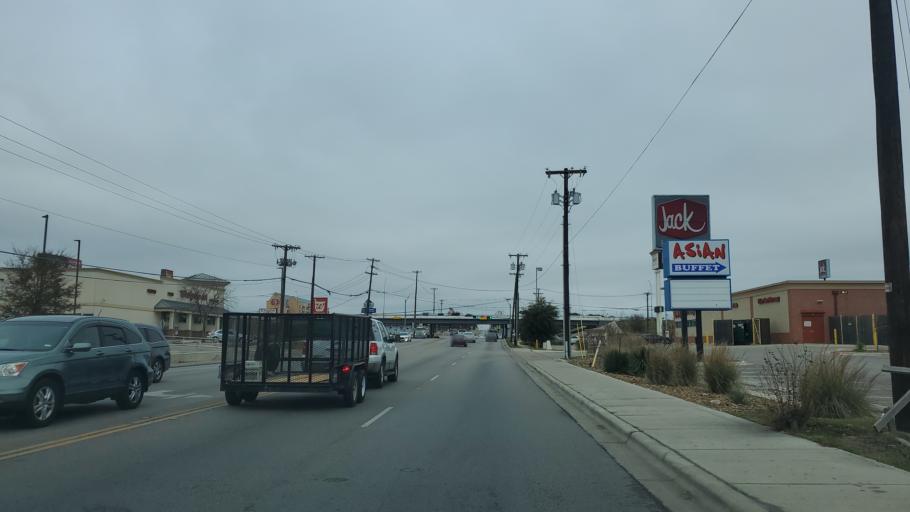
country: US
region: Texas
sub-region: Bell County
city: Killeen
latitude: 31.0926
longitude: -97.7330
